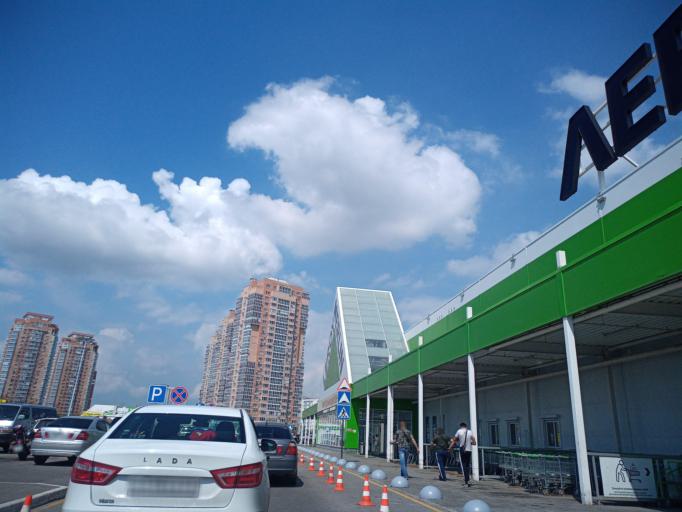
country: RU
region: Khabarovsk Krai
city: Khabarovsk Vtoroy
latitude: 48.4291
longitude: 135.1032
